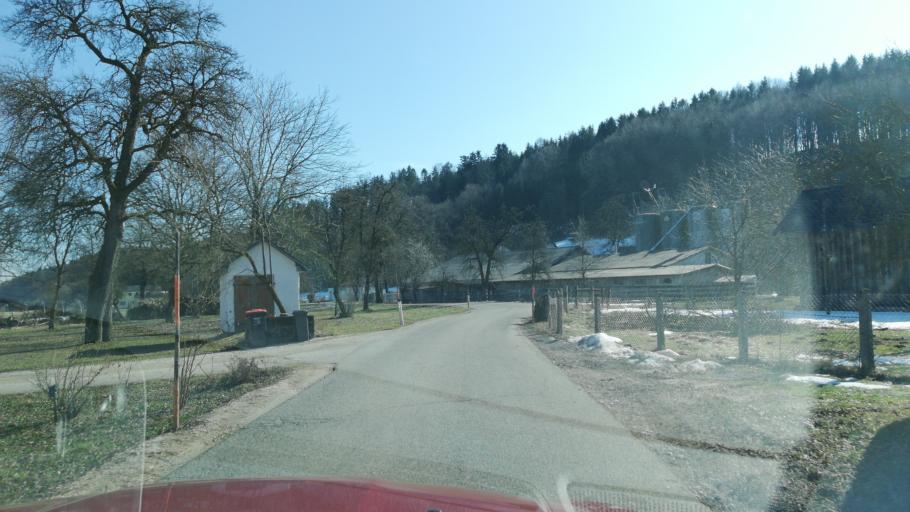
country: AT
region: Upper Austria
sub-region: Politischer Bezirk Vocklabruck
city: Vocklabruck
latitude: 47.9875
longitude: 13.6588
